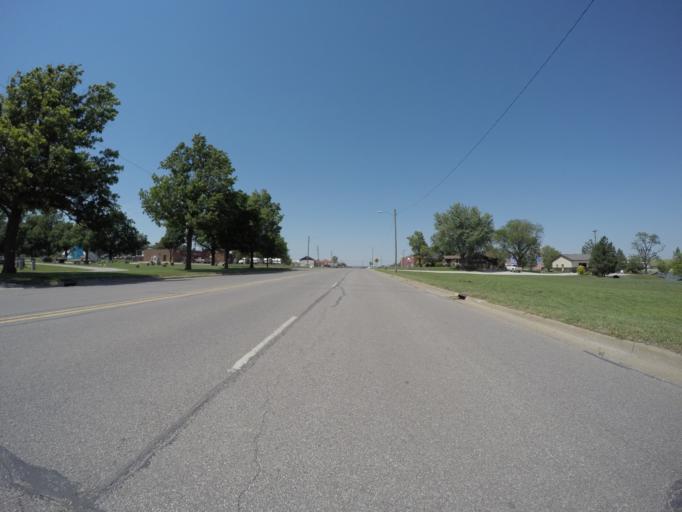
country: US
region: Kansas
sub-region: Nemaha County
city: Sabetha
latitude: 39.9018
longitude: -95.7882
